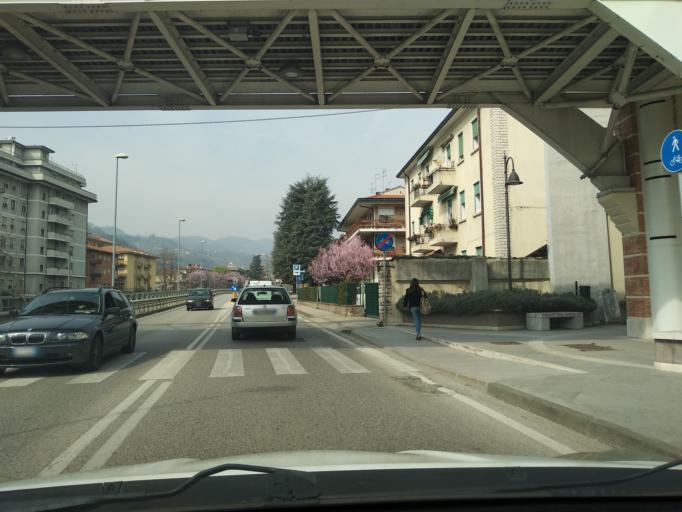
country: IT
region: Veneto
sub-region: Provincia di Vicenza
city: Chiampo
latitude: 45.5457
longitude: 11.2813
